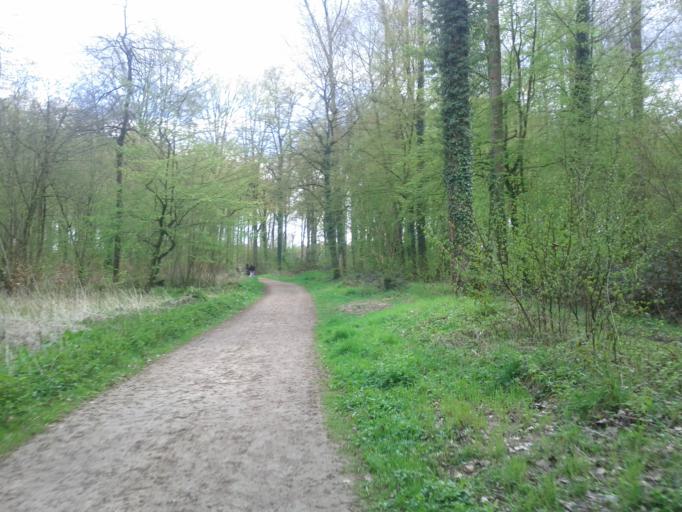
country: DE
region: North Rhine-Westphalia
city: Lanstrop
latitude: 51.5639
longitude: 7.5800
